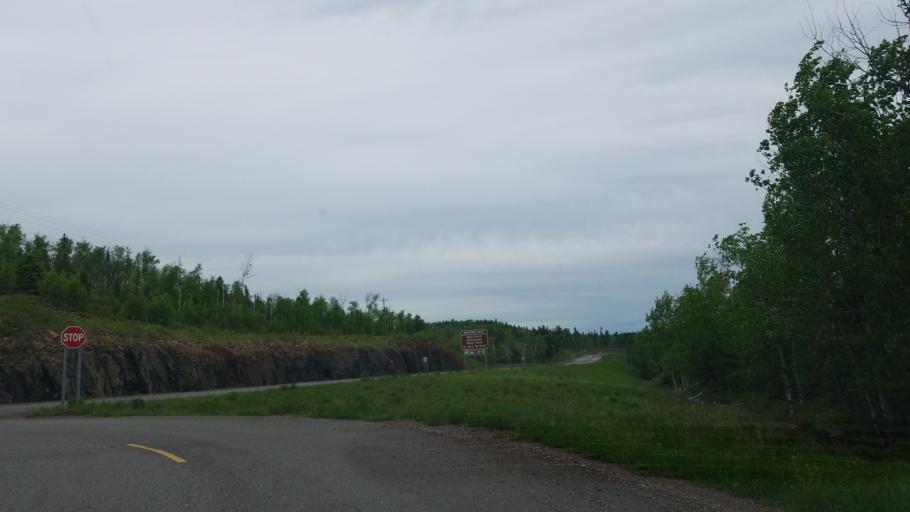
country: US
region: Minnesota
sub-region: Lake County
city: Silver Bay
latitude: 47.2000
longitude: -91.3790
